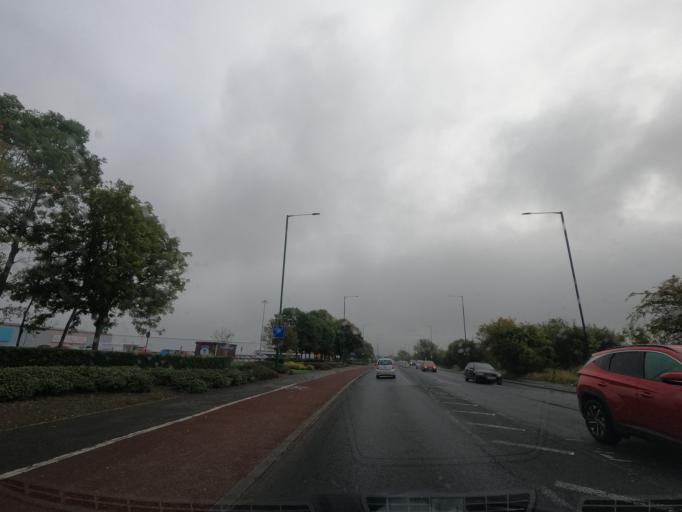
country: GB
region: England
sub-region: Redcar and Cleveland
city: South Bank
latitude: 54.5699
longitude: -1.1813
